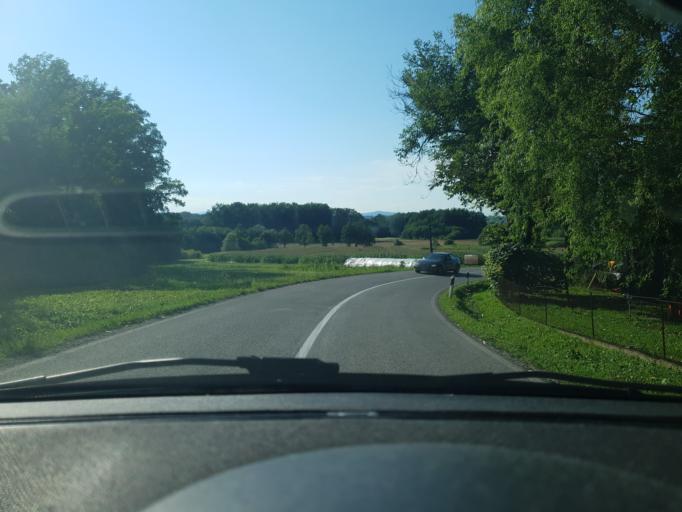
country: HR
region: Zagrebacka
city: Jakovlje
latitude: 45.9173
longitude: 15.8425
